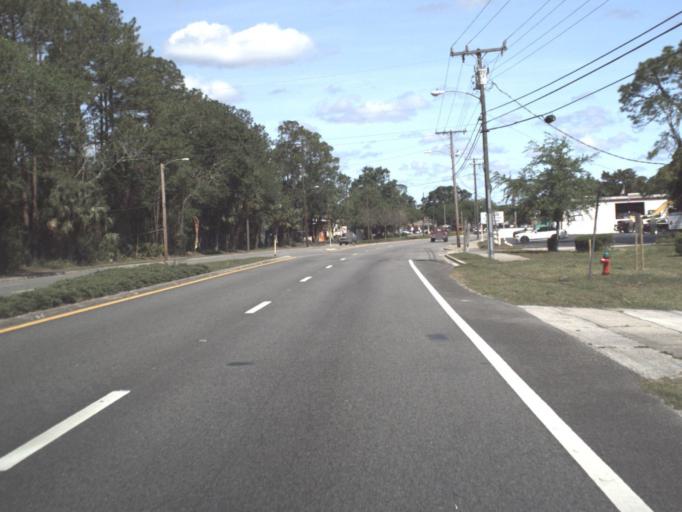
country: US
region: Florida
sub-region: Flagler County
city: Bunnell
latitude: 29.4579
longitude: -81.2507
